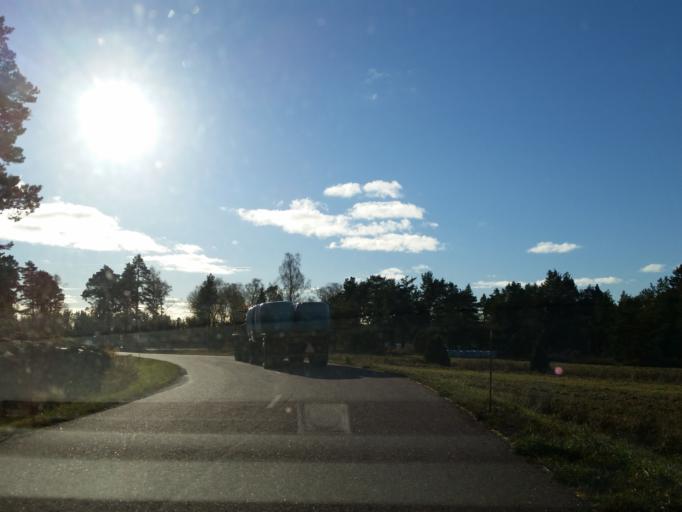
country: AX
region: Alands landsbygd
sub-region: Geta
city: Geta
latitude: 60.3659
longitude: 19.7907
